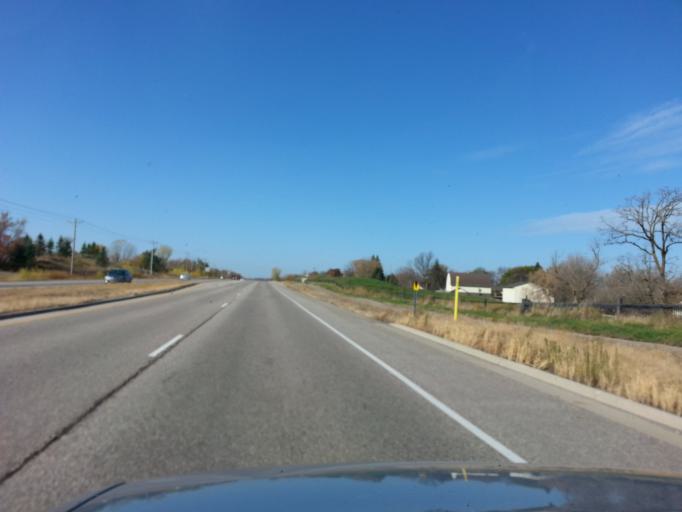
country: US
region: Minnesota
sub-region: Dakota County
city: Lakeville
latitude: 44.6815
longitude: -93.3297
